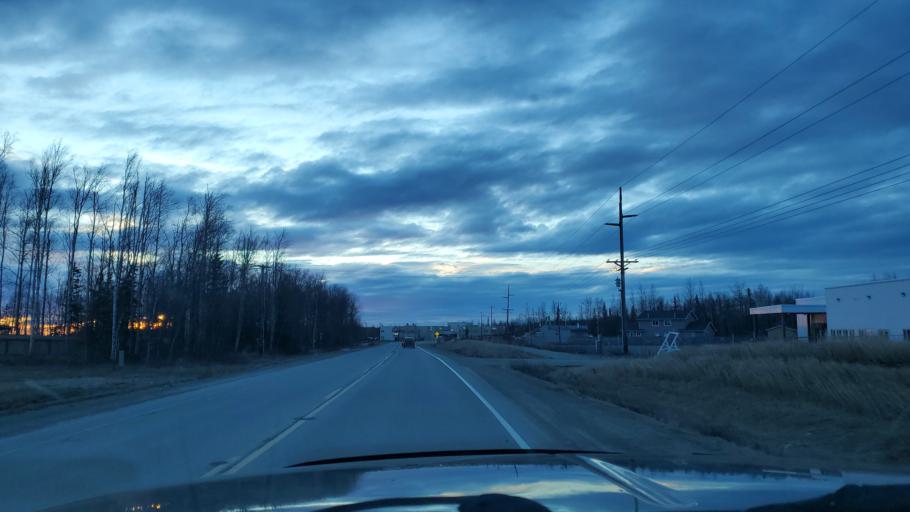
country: US
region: Alaska
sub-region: Matanuska-Susitna Borough
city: Wasilla
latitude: 61.5907
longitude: -149.3991
